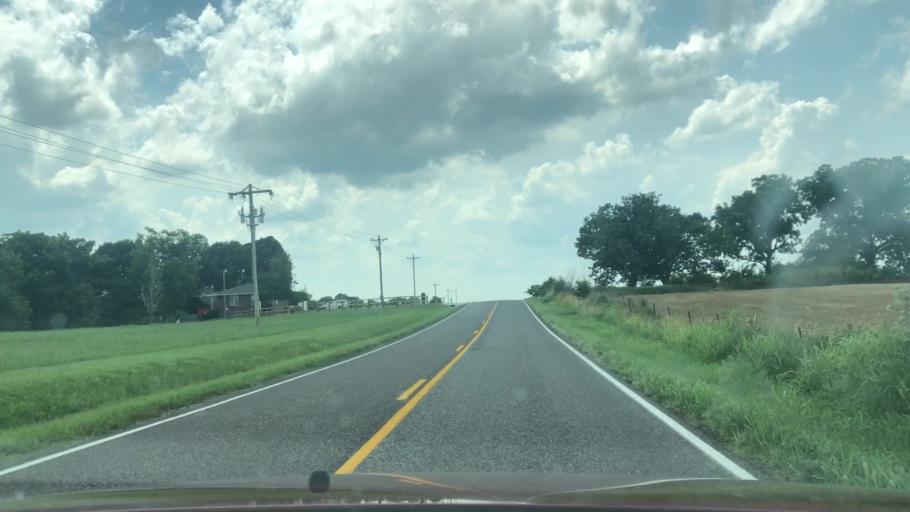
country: US
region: Missouri
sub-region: Christian County
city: Ozark
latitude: 36.9431
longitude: -93.2445
